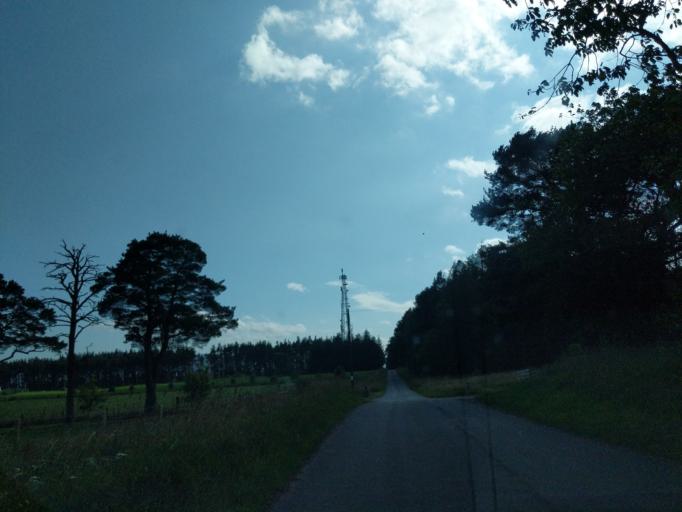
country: GB
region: Scotland
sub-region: Moray
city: Rothes
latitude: 57.4855
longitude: -3.2295
